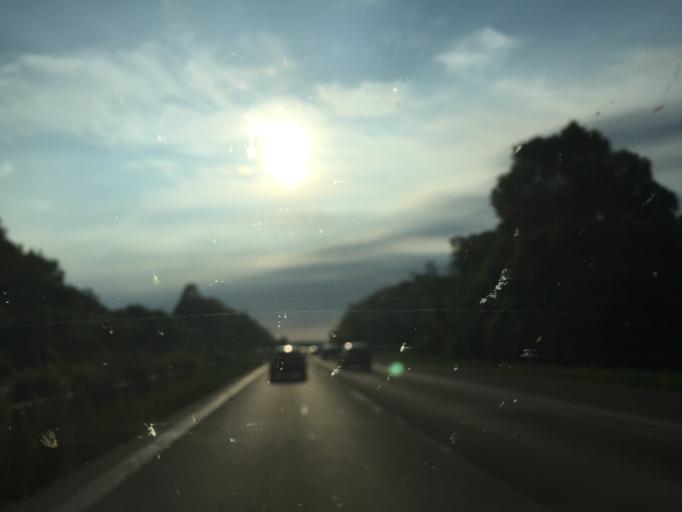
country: DE
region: Baden-Wuerttemberg
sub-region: Karlsruhe Region
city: Balzfeld
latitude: 49.2587
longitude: 8.8195
